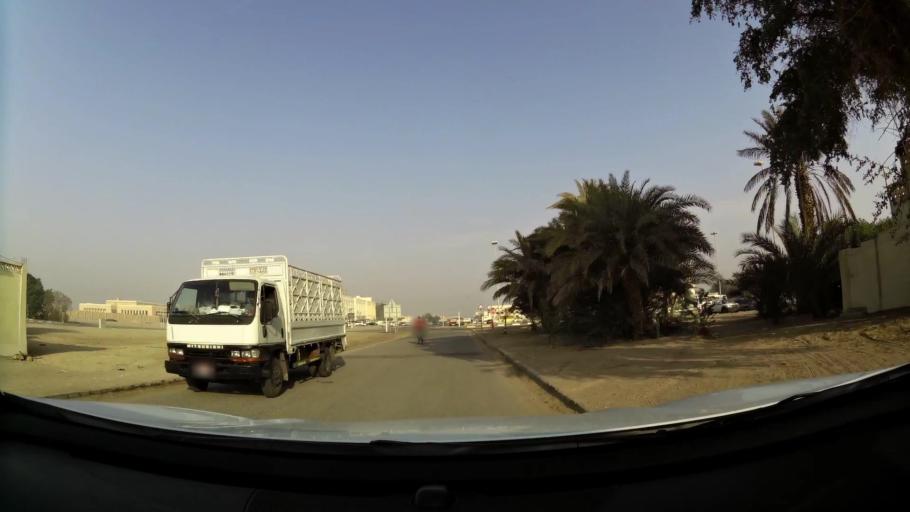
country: AE
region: Abu Dhabi
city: Abu Dhabi
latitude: 24.2935
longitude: 54.6281
